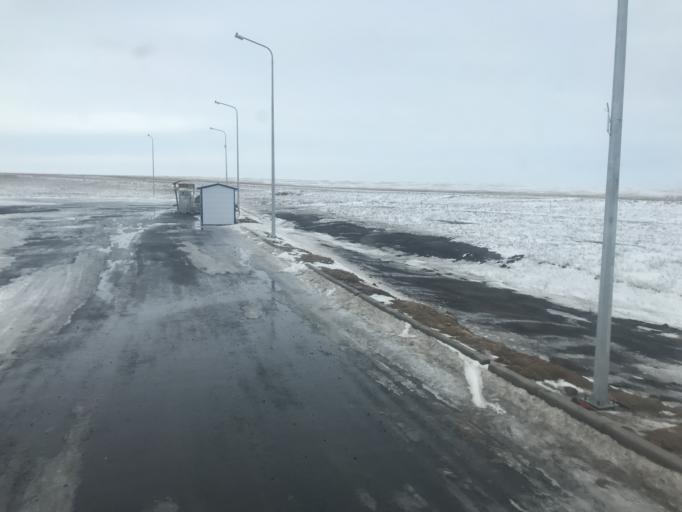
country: KZ
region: Batys Qazaqstan
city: Oral
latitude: 51.4035
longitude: 51.2976
